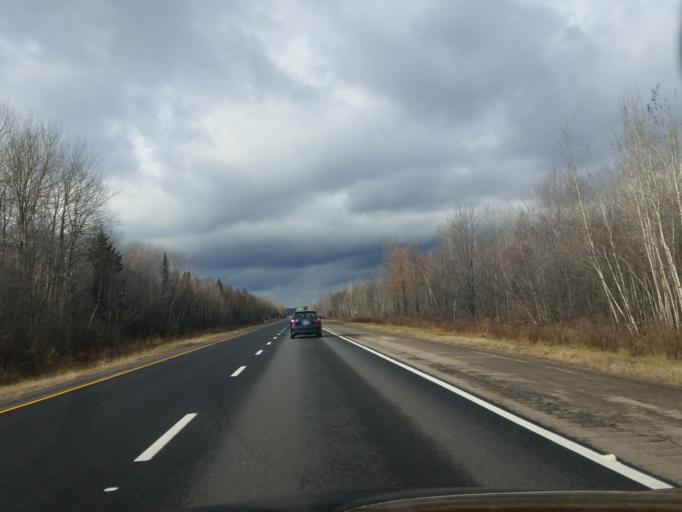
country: CA
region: Quebec
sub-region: Capitale-Nationale
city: Cap-Sante
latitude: 46.6969
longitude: -71.8268
